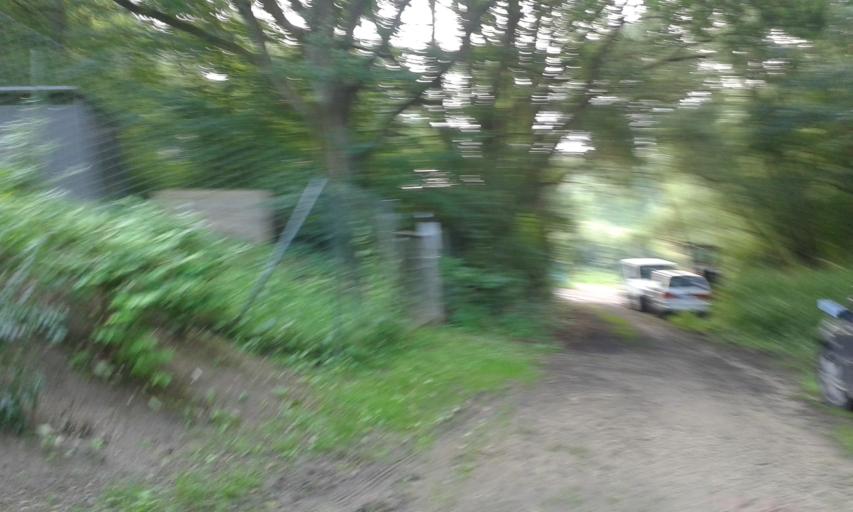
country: DE
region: Bavaria
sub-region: Upper Franconia
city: Bamberg
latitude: 49.8728
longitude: 10.8984
